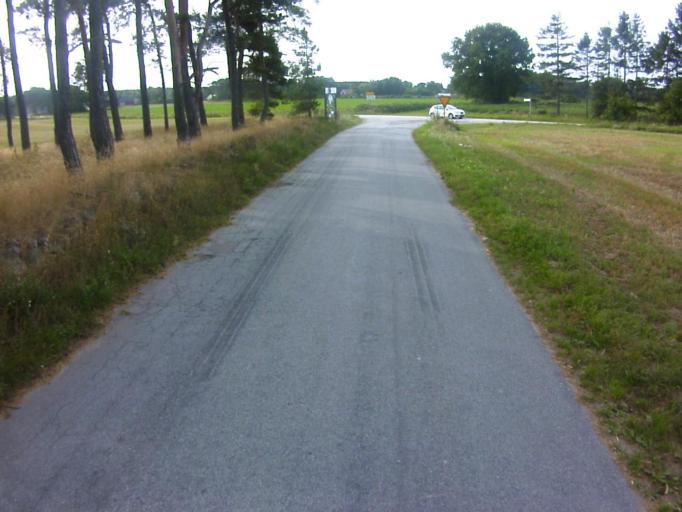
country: SE
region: Blekinge
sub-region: Solvesborgs Kommun
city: Soelvesborg
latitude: 56.0267
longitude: 14.7129
